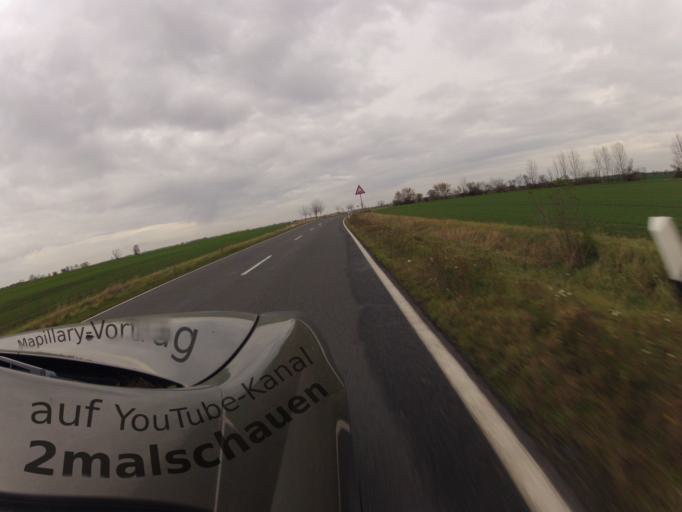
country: DE
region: Saxony-Anhalt
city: Beesenlaublingen
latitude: 51.7233
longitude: 11.7240
